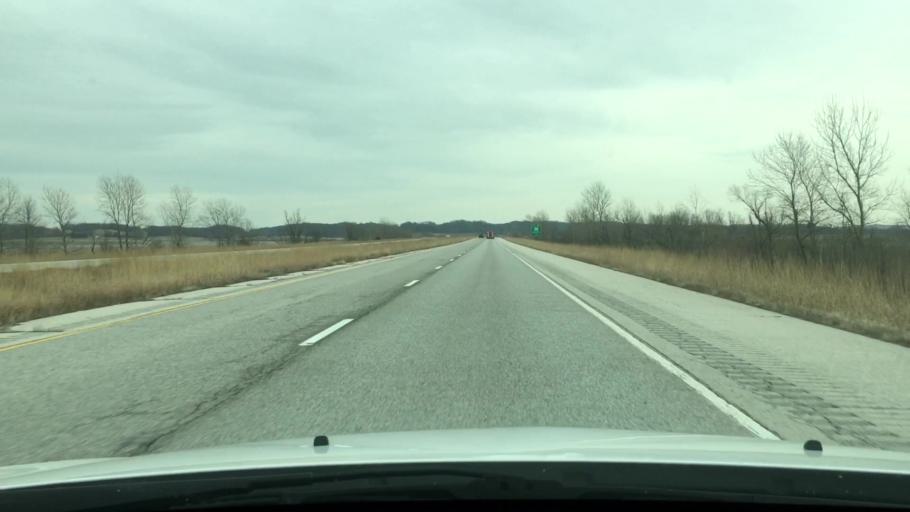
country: US
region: Illinois
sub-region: Pike County
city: Griggsville
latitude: 39.6898
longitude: -90.6021
